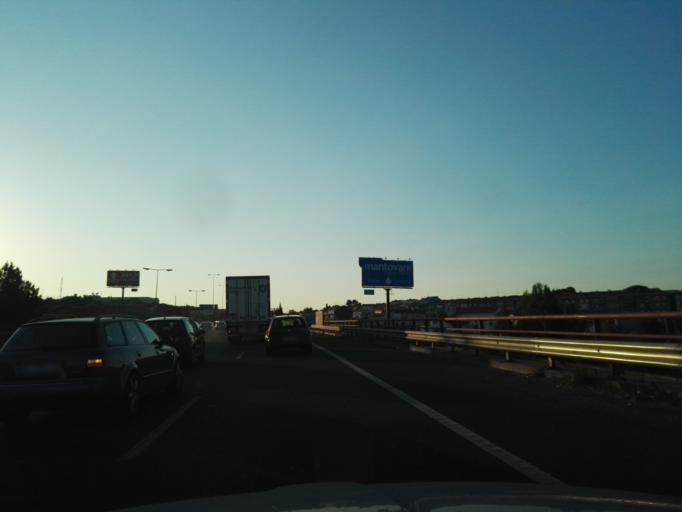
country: PT
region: Lisbon
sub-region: Loures
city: Camarate
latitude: 38.7998
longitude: -9.1269
